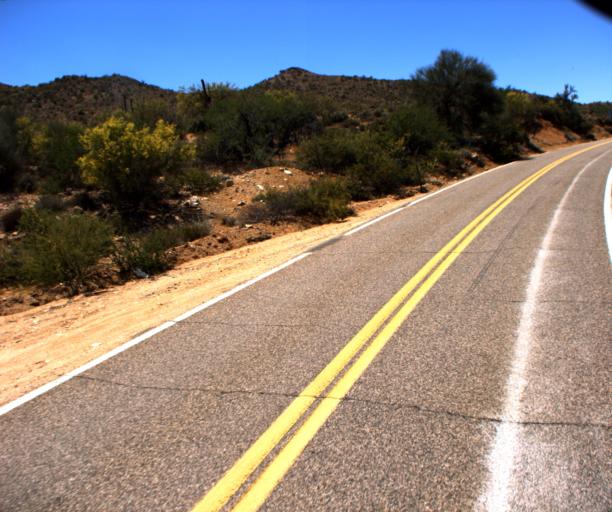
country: US
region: Arizona
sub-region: Yavapai County
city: Bagdad
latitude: 34.4593
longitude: -113.0358
